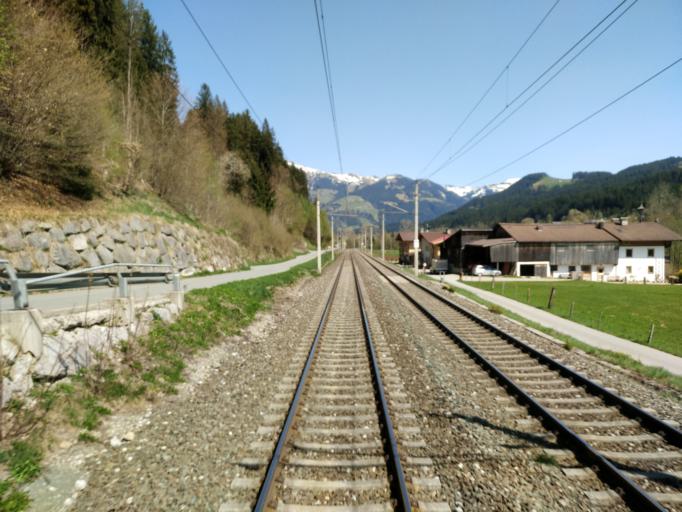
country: AT
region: Tyrol
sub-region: Politischer Bezirk Kitzbuhel
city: Kirchberg in Tirol
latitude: 47.4516
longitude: 12.3242
